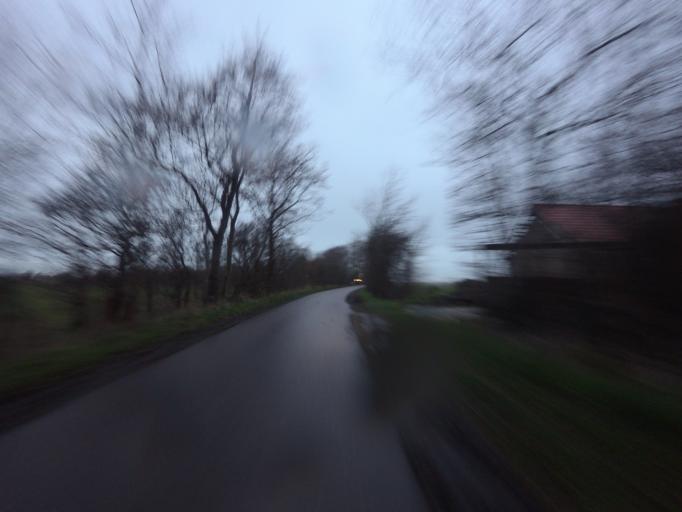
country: NL
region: North Holland
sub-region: Gemeente Texel
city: Den Burg
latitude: 53.0646
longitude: 4.8028
